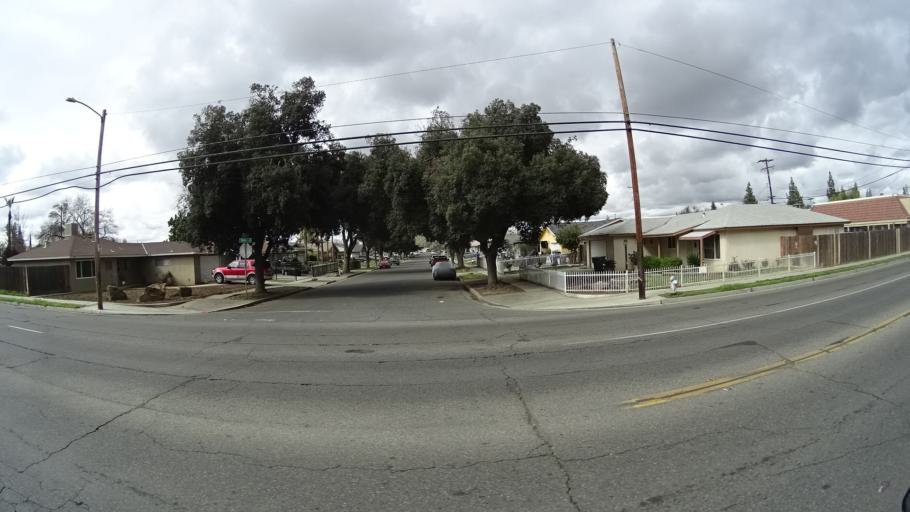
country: US
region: California
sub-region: Fresno County
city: West Park
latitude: 36.7923
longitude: -119.8443
